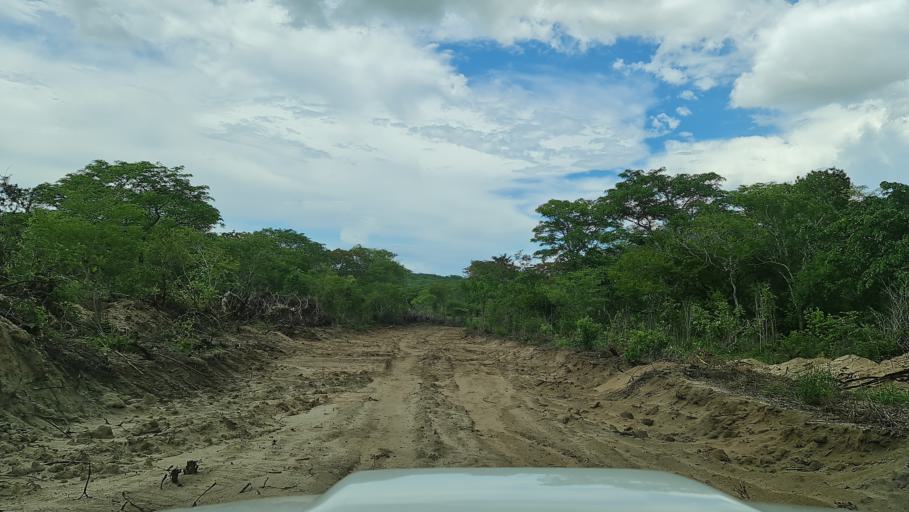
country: MZ
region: Nampula
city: Ilha de Mocambique
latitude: -15.5104
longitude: 40.1931
